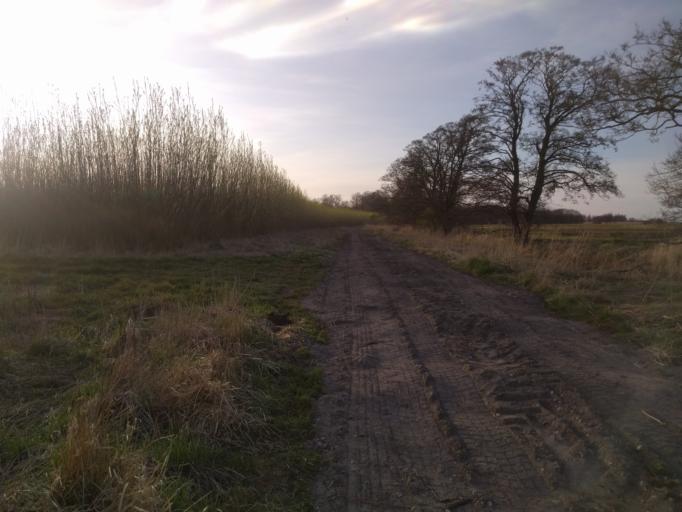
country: DK
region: South Denmark
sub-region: Kerteminde Kommune
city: Munkebo
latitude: 55.4124
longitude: 10.5497
